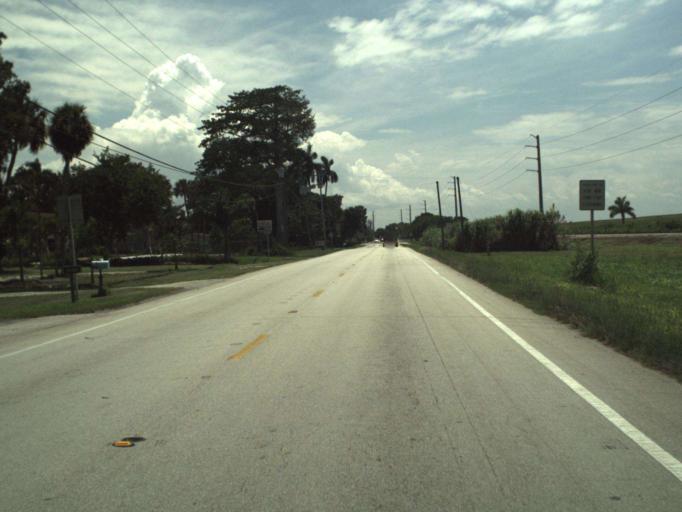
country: US
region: Florida
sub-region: Palm Beach County
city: Pahokee
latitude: 26.8696
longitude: -80.6269
